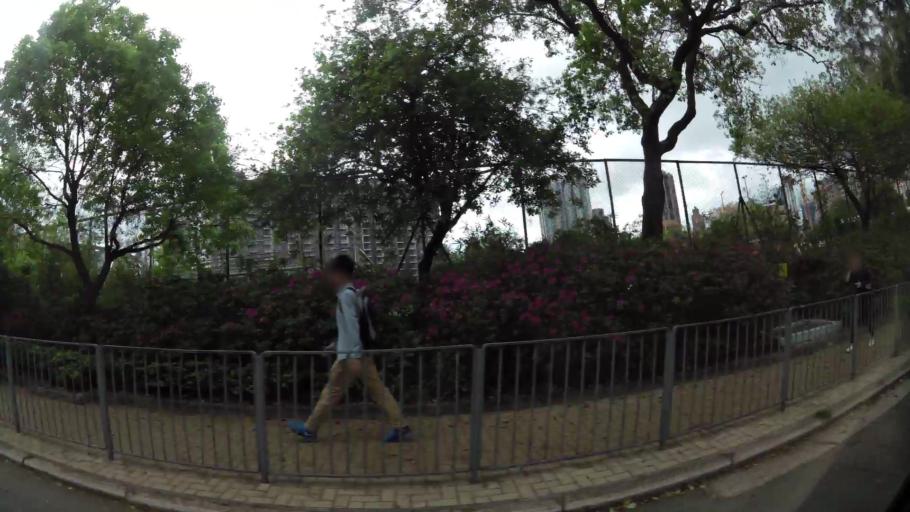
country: HK
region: Kowloon City
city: Kowloon
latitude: 22.3229
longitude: 114.1844
